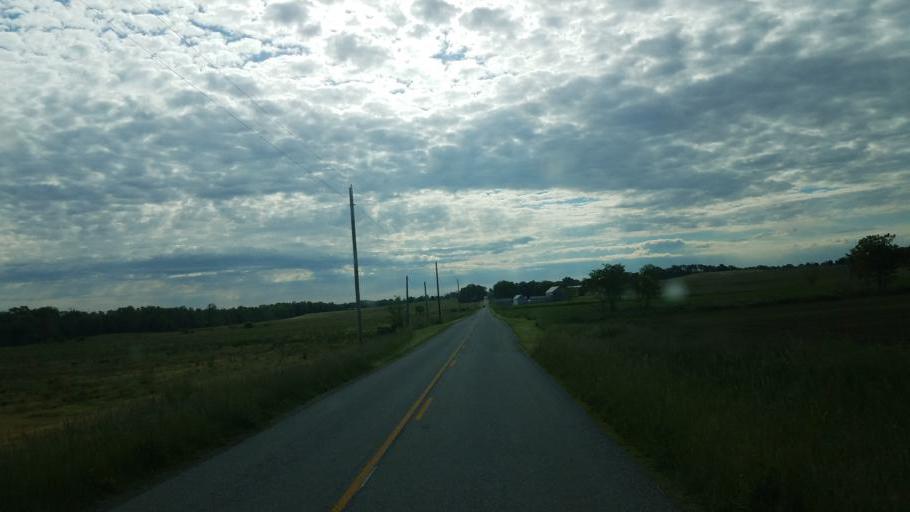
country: US
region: Ohio
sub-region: Medina County
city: Lodi
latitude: 40.9885
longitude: -81.9816
